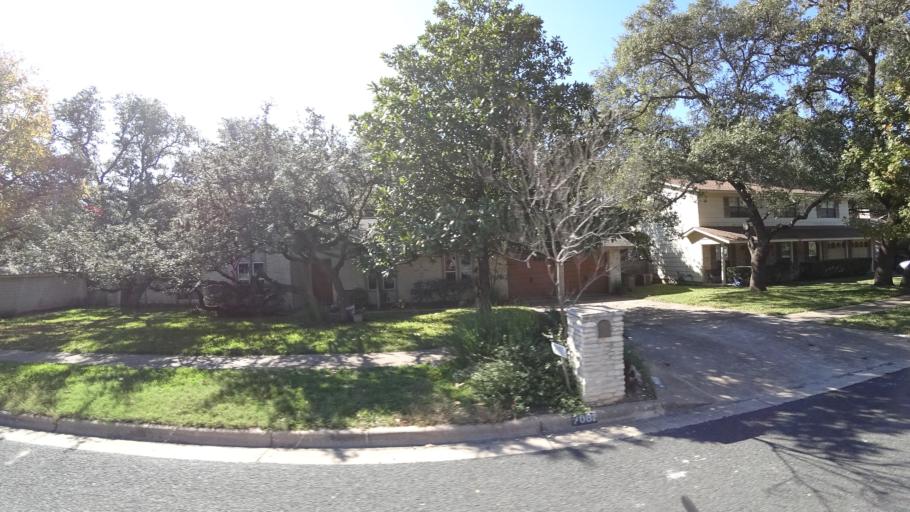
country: US
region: Texas
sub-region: Williamson County
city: Jollyville
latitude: 30.4243
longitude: -97.7661
